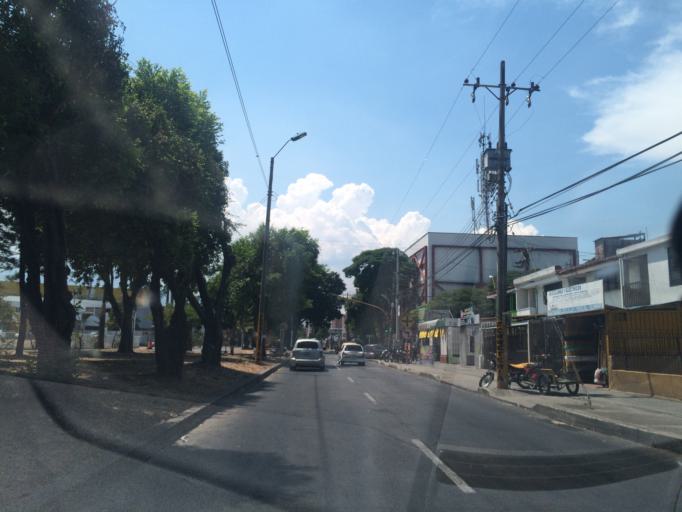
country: CO
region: Valle del Cauca
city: Cali
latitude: 3.4711
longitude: -76.5026
